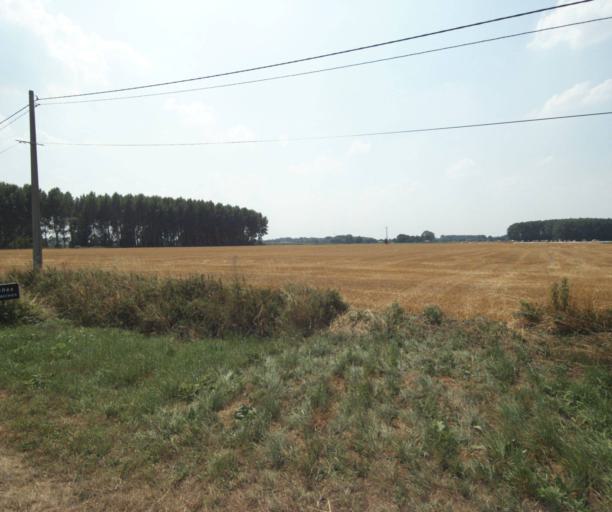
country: FR
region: Nord-Pas-de-Calais
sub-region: Departement du Nord
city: Wambrechies
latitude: 50.7055
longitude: 3.0340
